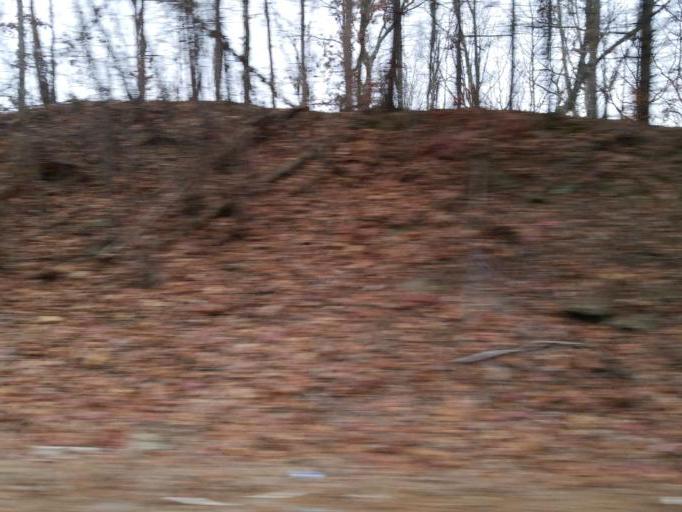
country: US
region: Georgia
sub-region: Dawson County
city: Dawsonville
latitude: 34.4036
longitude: -84.0145
